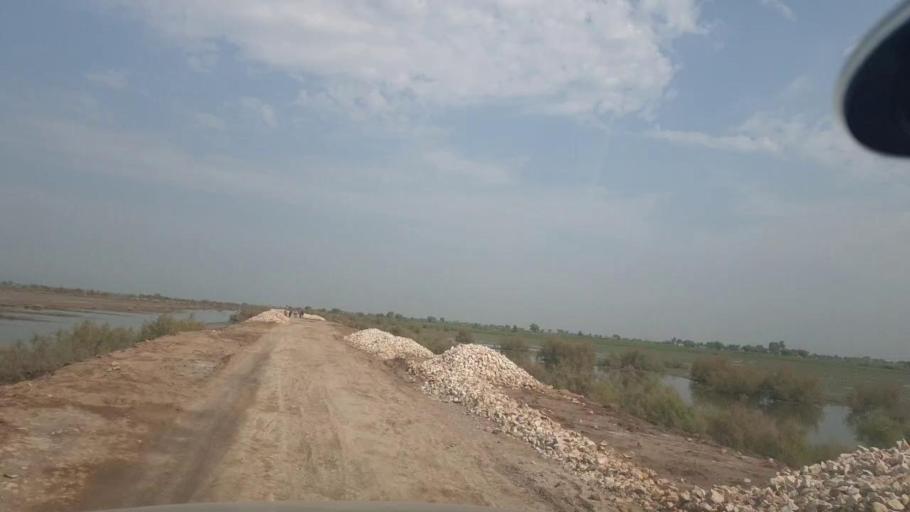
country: PK
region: Balochistan
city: Mehrabpur
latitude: 28.0829
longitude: 68.0995
